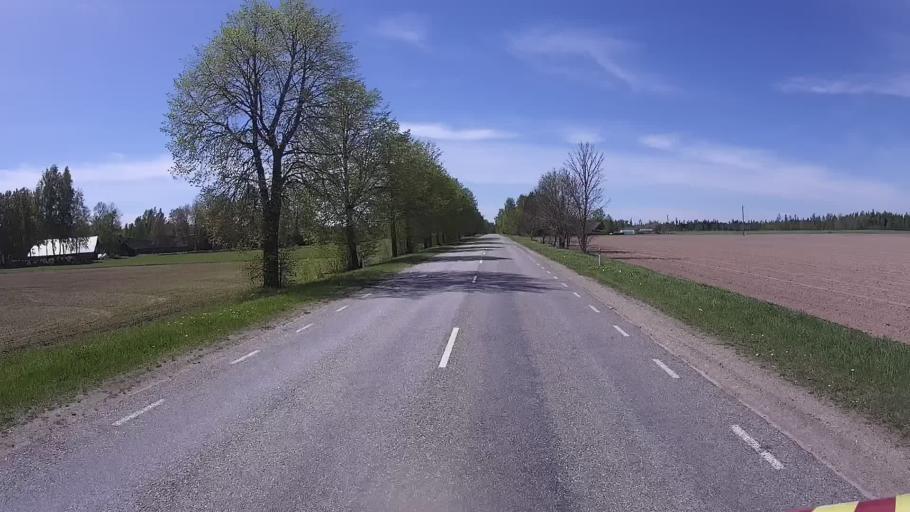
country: EE
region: Polvamaa
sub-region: Raepina vald
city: Rapina
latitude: 57.9897
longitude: 27.3265
